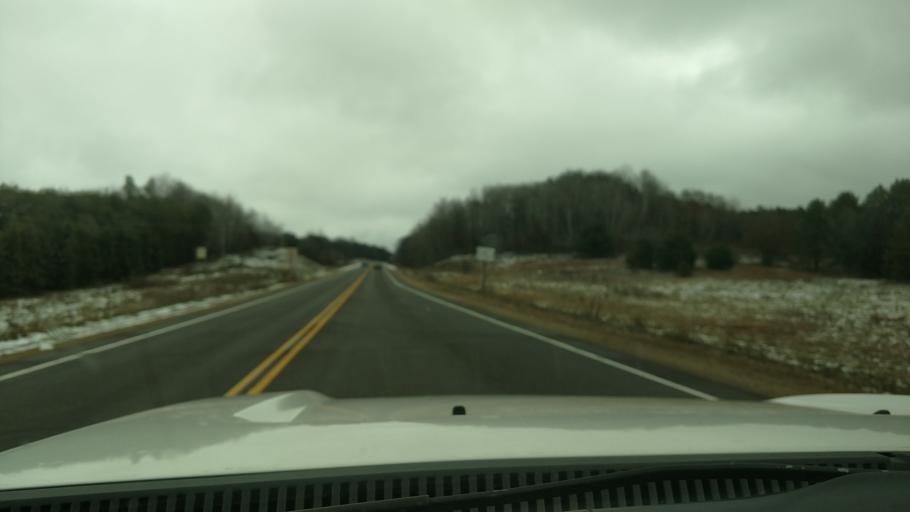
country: US
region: Wisconsin
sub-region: Dunn County
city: Tainter Lake
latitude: 45.1250
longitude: -91.9114
